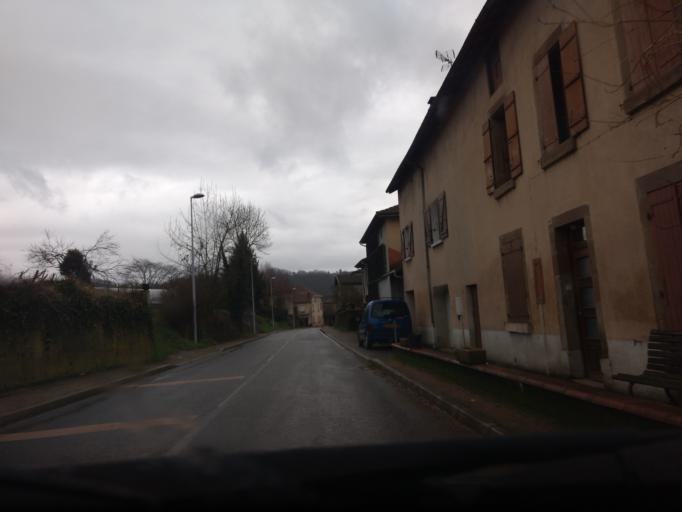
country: FR
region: Midi-Pyrenees
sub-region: Departement de l'Aveyron
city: Livinhac-le-Haut
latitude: 44.5900
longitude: 2.2310
